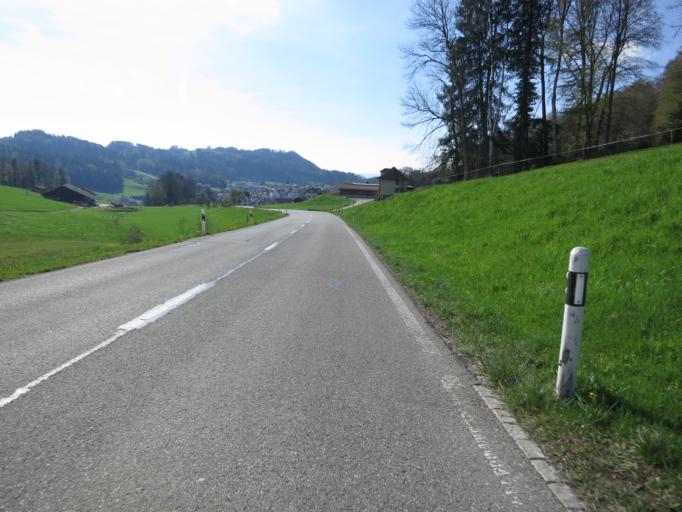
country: CH
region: Saint Gallen
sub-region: Wahlkreis See-Gaster
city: Goldingen
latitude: 47.2660
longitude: 8.9410
